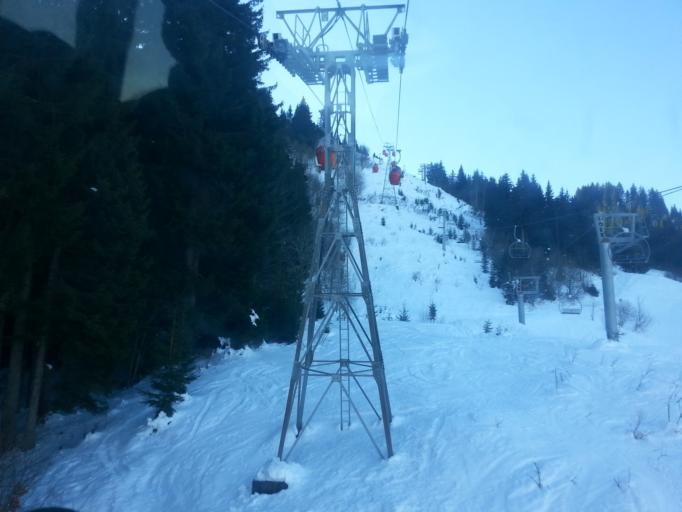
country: FR
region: Rhone-Alpes
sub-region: Departement de la Haute-Savoie
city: Samoens
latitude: 46.0614
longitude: 6.6994
